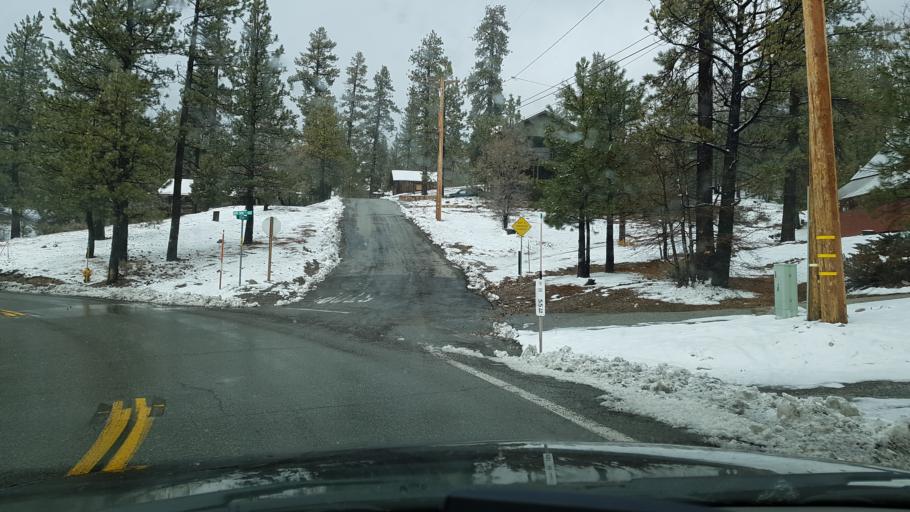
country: US
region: California
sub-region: San Bernardino County
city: Big Bear Lake
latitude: 34.2668
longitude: -116.9407
